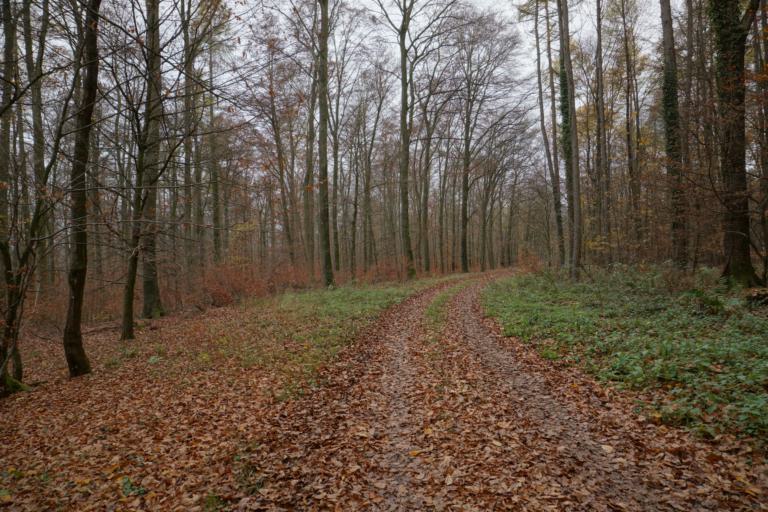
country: DE
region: Baden-Wuerttemberg
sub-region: Karlsruhe Region
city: Huffenhardt
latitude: 49.3046
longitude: 9.0405
